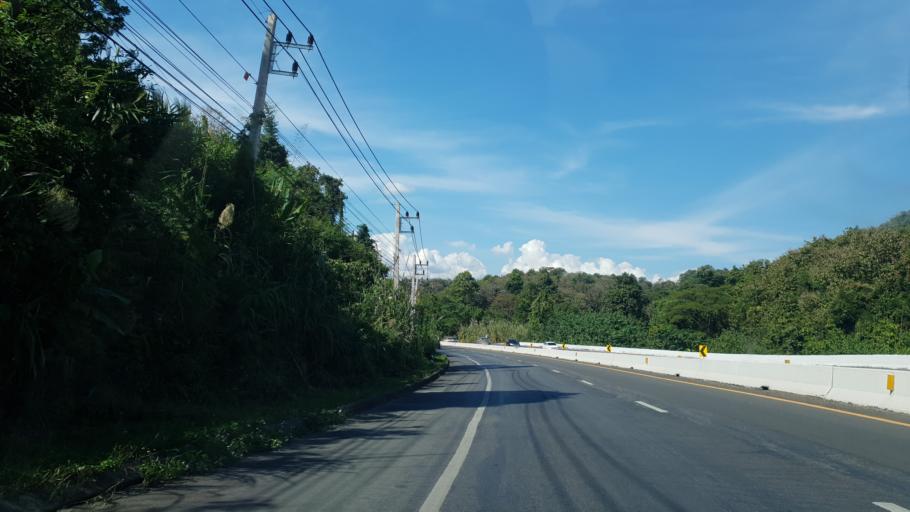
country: TH
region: Phrae
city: Den Chai
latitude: 17.8452
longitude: 100.0510
